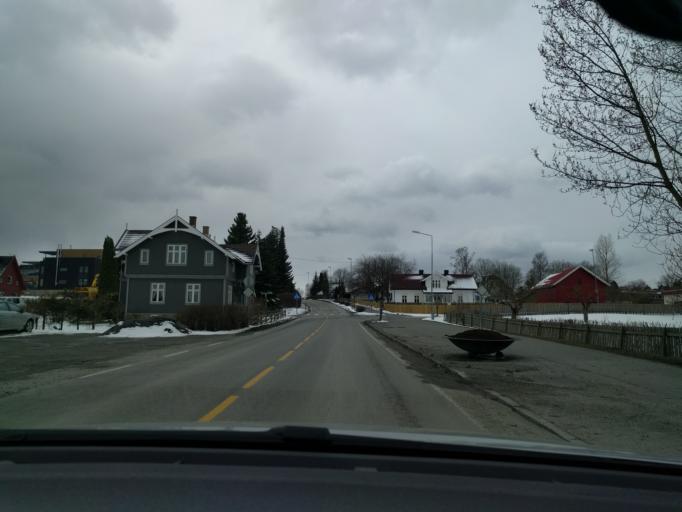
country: NO
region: Hedmark
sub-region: Stange
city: Stange
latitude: 60.7172
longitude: 11.1890
